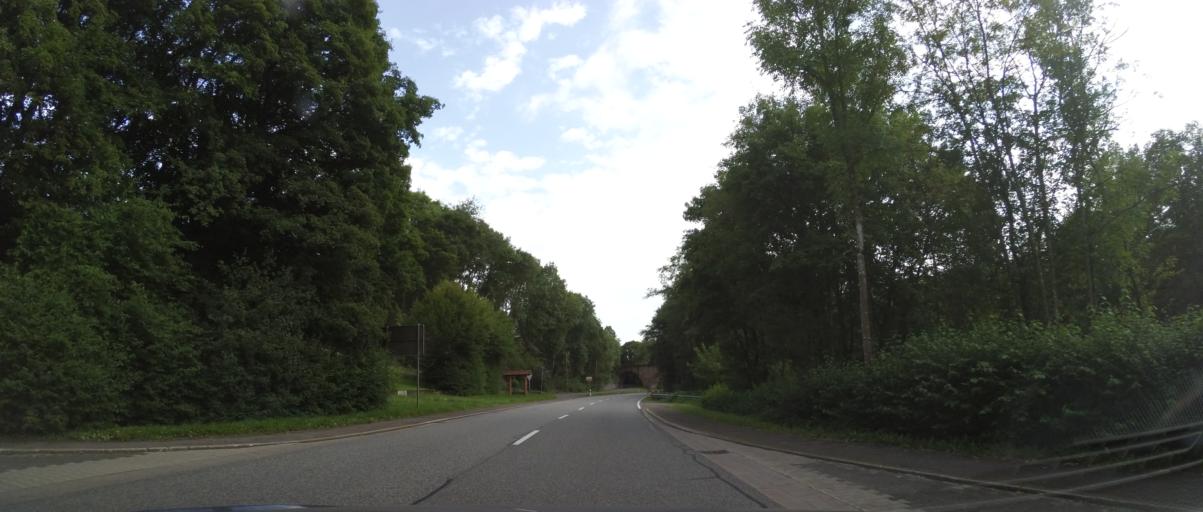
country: DE
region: Saarland
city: Nonnweiler
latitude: 49.6052
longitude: 6.9737
